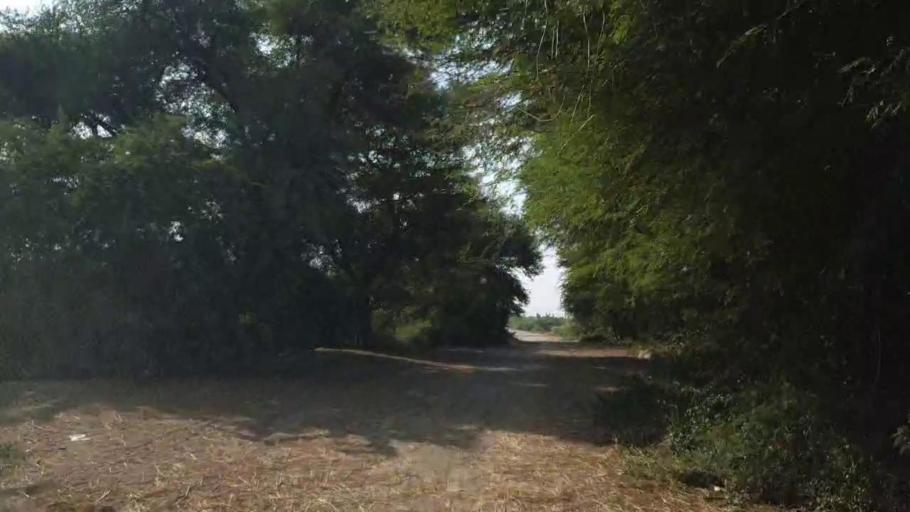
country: PK
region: Sindh
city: Tando Muhammad Khan
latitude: 25.0602
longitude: 68.4139
